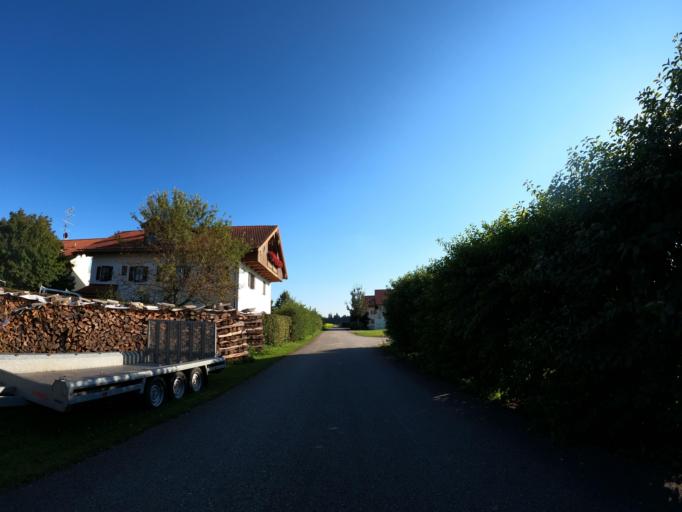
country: DE
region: Bavaria
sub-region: Upper Bavaria
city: Grasbrunn
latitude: 48.0564
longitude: 11.7736
